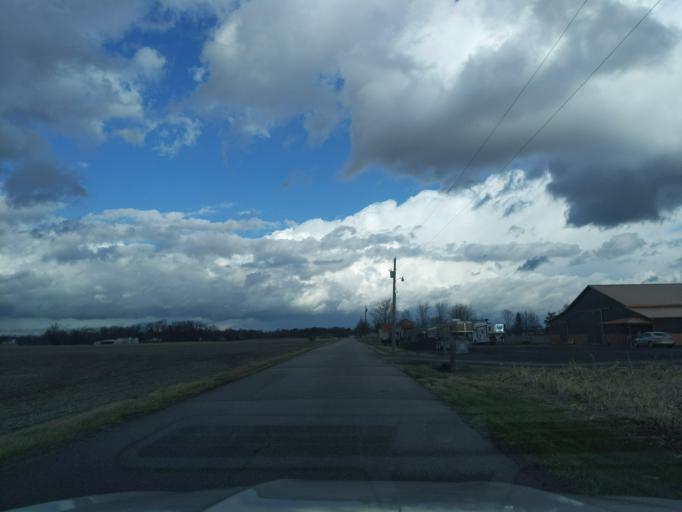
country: US
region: Indiana
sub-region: Decatur County
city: Saint Paul
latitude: 39.3961
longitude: -85.5599
